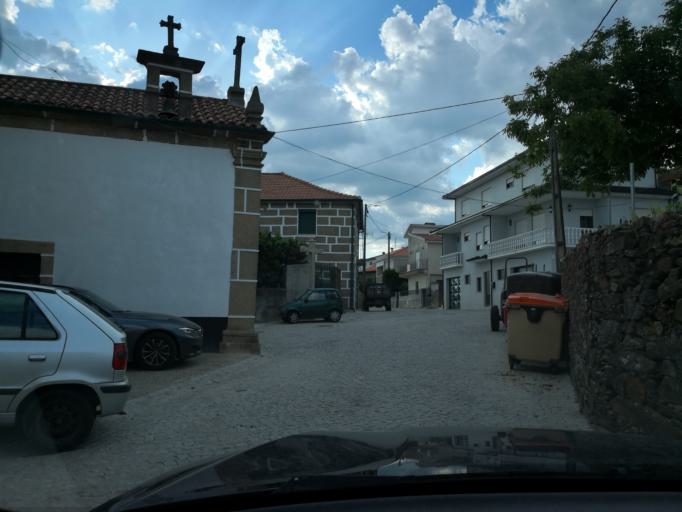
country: PT
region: Vila Real
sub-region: Sabrosa
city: Vilela
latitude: 41.2083
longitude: -7.6616
